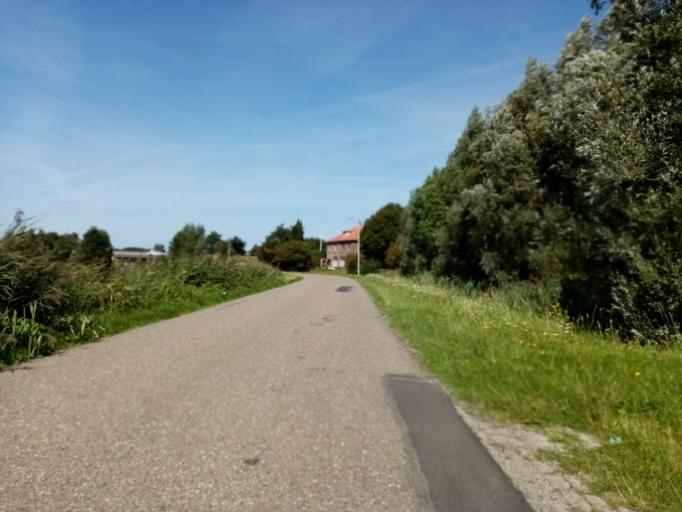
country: NL
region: South Holland
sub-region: Gemeente Noordwijkerhout
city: Noordwijkerhout
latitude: 52.2832
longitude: 4.5205
